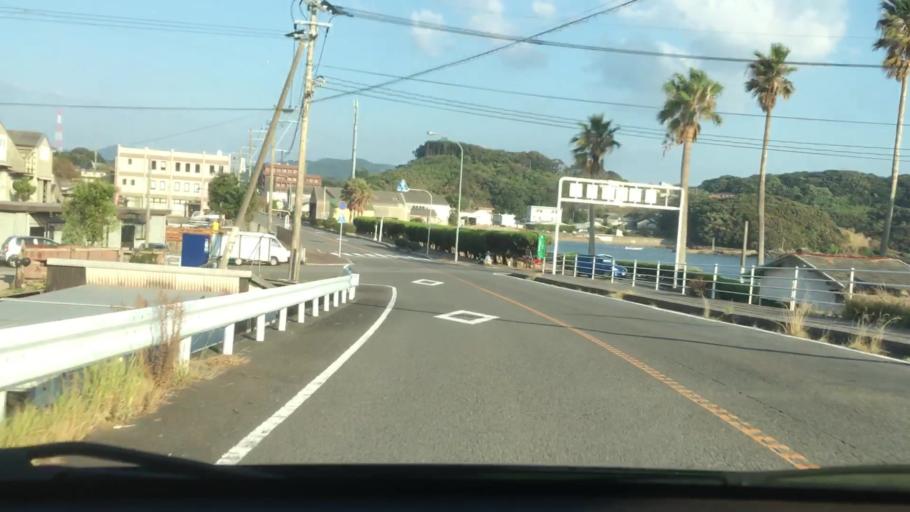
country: JP
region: Nagasaki
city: Sasebo
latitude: 33.0347
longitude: 129.6141
